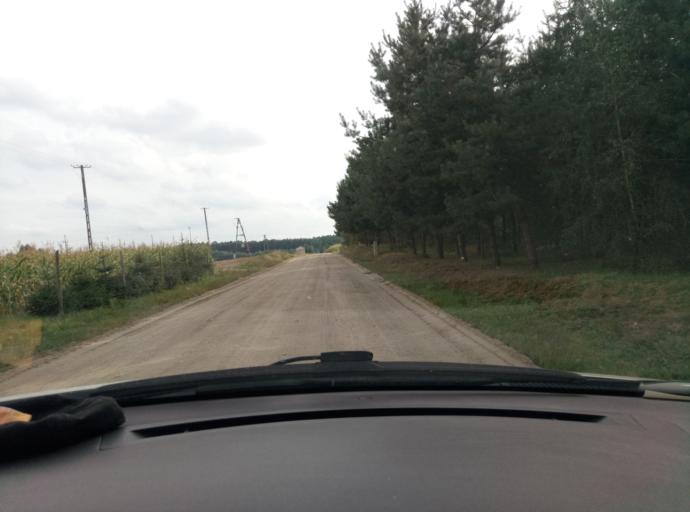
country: PL
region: Warmian-Masurian Voivodeship
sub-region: Powiat nowomiejski
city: Biskupiec
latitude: 53.4135
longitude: 19.2724
